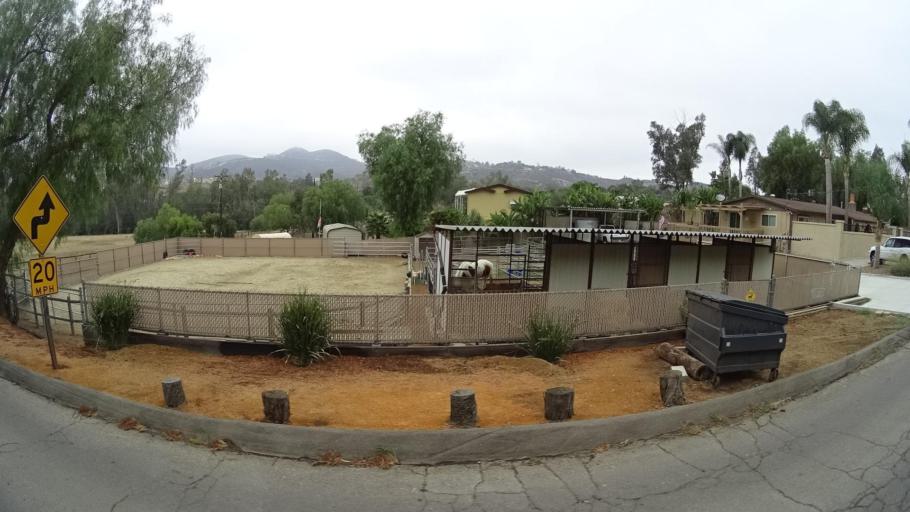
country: US
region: California
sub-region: San Diego County
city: Escondido
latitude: 33.1131
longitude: -117.1274
